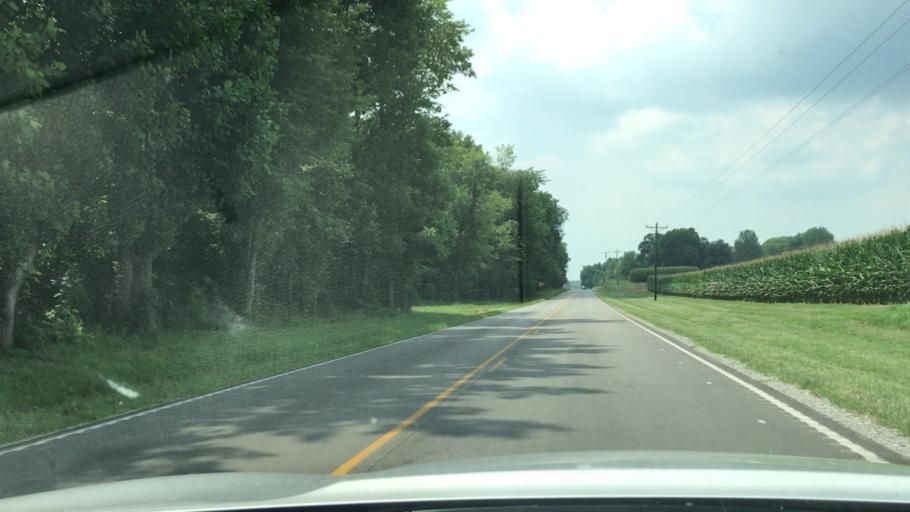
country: US
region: Kentucky
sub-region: Todd County
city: Guthrie
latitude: 36.7087
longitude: -87.1036
